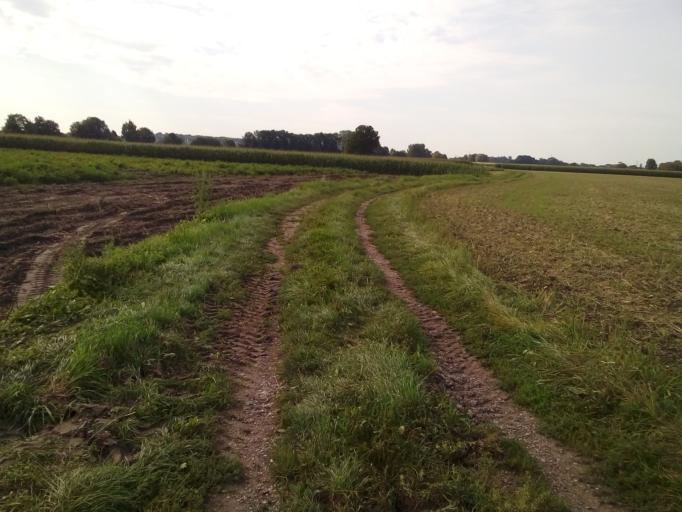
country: DE
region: Bavaria
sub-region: Upper Bavaria
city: Ismaning
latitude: 48.2254
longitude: 11.6991
